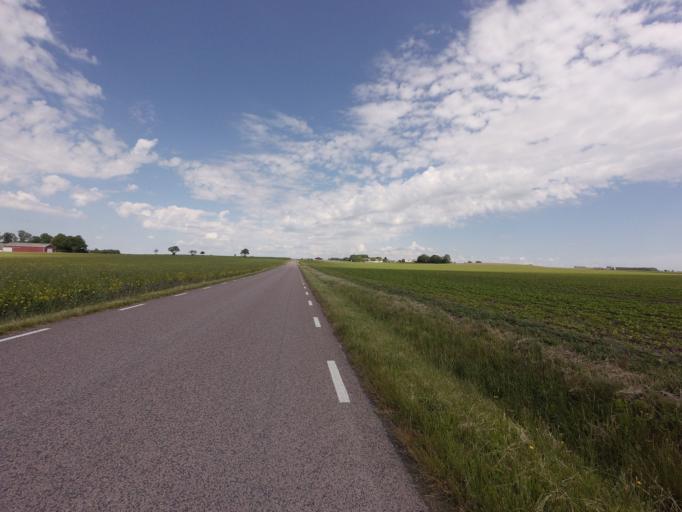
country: SE
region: Skane
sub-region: Trelleborgs Kommun
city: Skare
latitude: 55.4190
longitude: 13.1032
